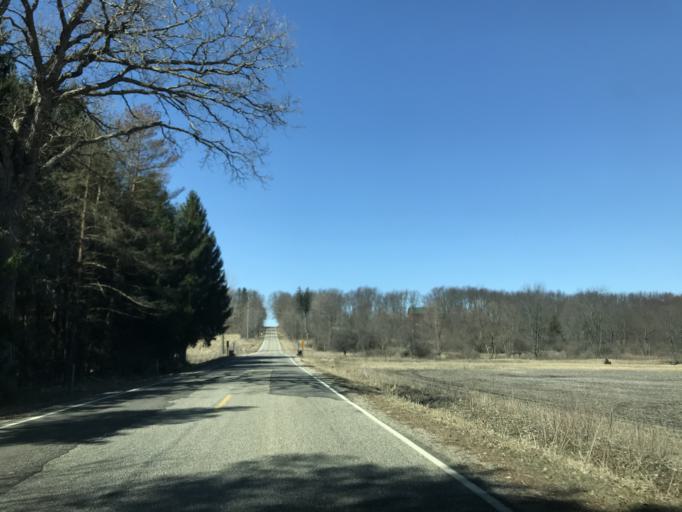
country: US
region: Michigan
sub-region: Hillsdale County
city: Litchfield
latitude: 41.9856
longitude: -84.7499
